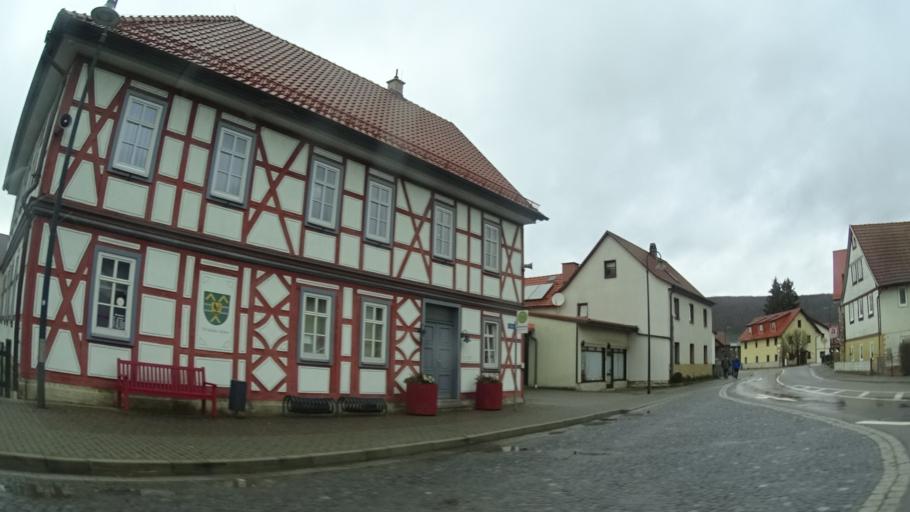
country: DE
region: Thuringia
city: Juchsen
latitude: 50.4809
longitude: 10.5016
